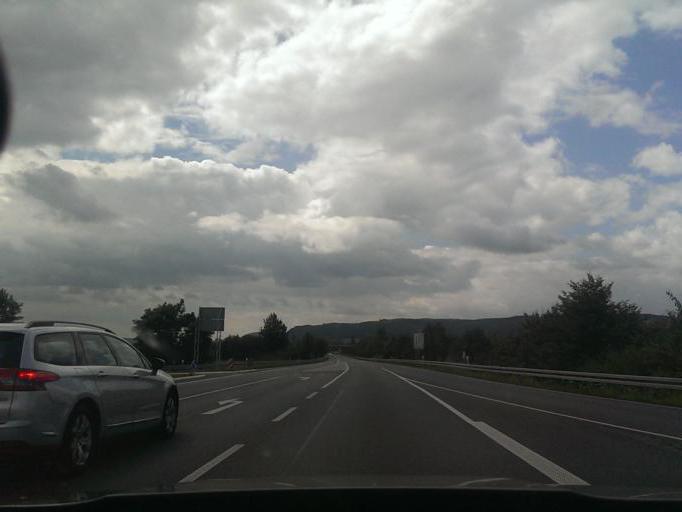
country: DE
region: Lower Saxony
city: Holzminden
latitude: 51.8309
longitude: 9.4331
